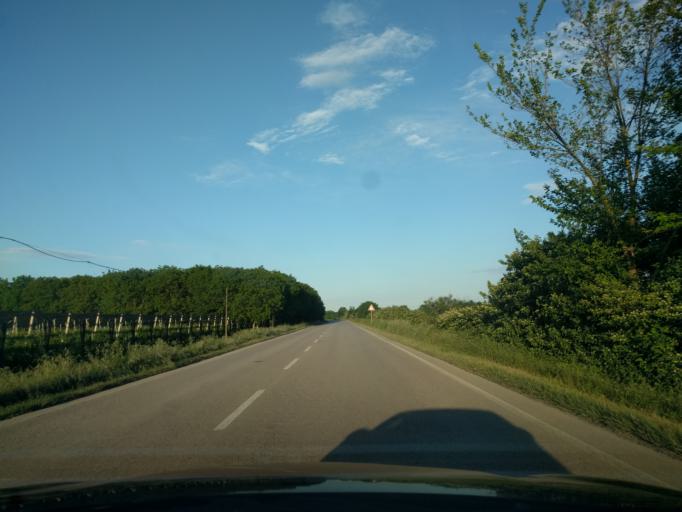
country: IT
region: Veneto
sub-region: Provincia di Rovigo
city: Guarda Veneta
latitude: 44.9829
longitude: 11.8310
